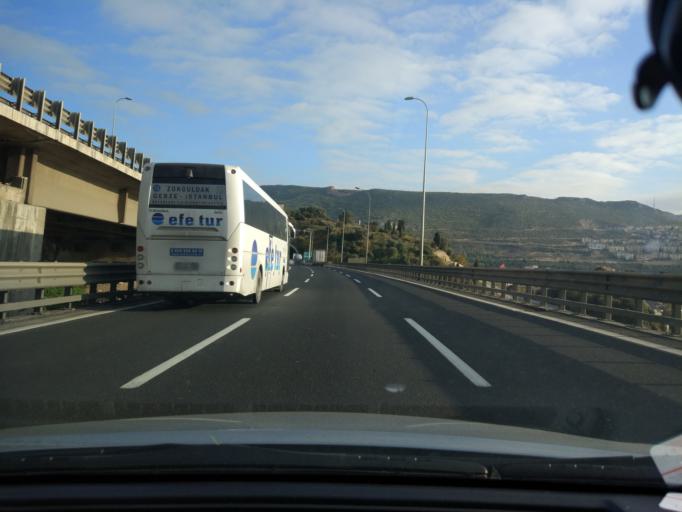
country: TR
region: Kocaeli
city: Hereke
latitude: 40.7822
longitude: 29.6066
